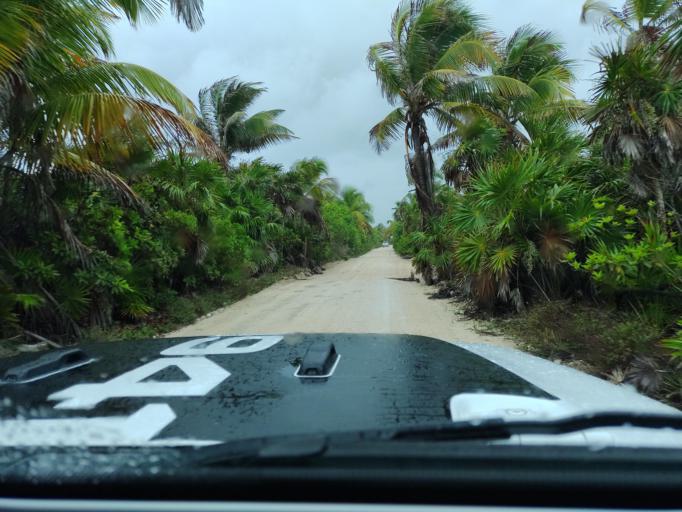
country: MX
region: Quintana Roo
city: Tulum
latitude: 19.9877
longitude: -87.4649
